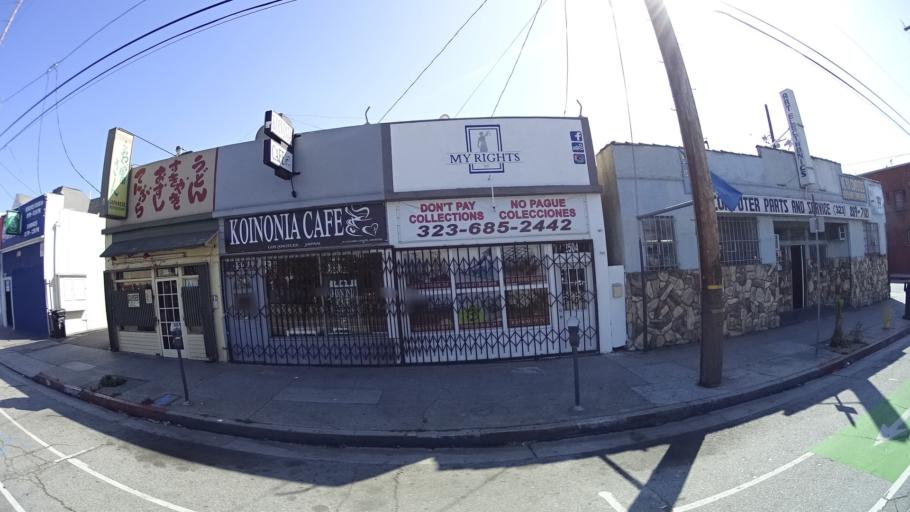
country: US
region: California
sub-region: Los Angeles County
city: Boyle Heights
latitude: 34.0431
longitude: -118.2085
